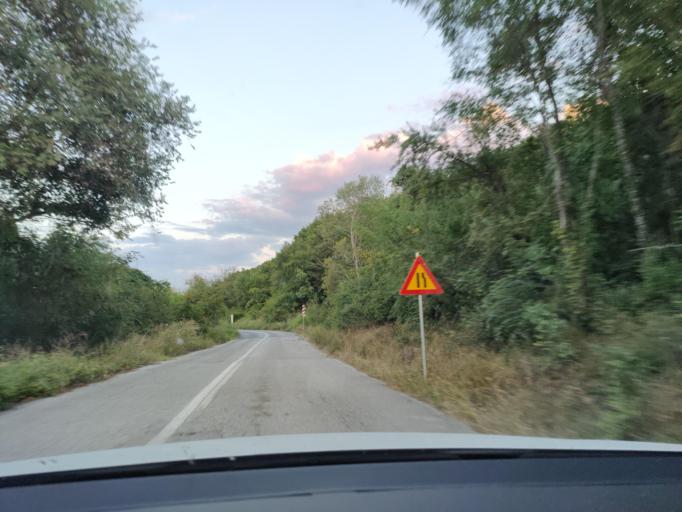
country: GR
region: Central Macedonia
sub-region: Nomos Serron
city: Chrysochorafa
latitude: 41.1809
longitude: 23.1513
